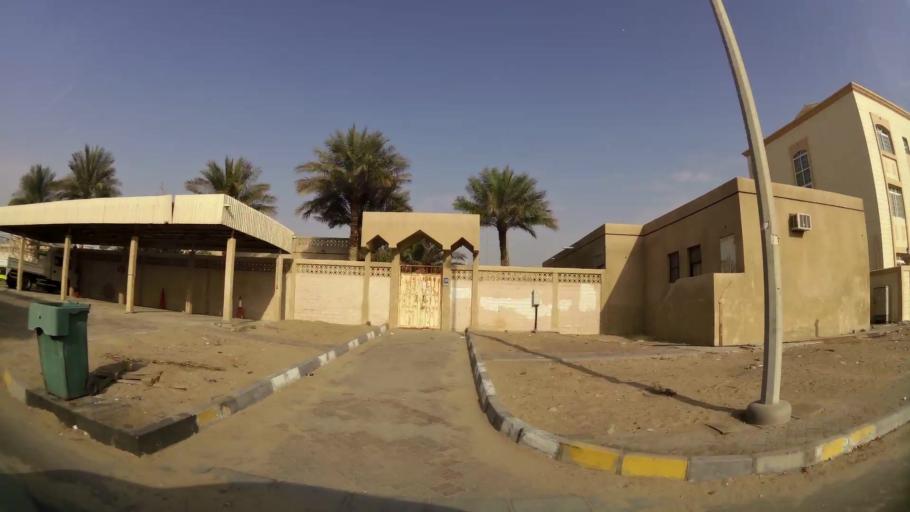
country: AE
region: Abu Dhabi
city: Abu Dhabi
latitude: 24.2717
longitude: 54.6425
